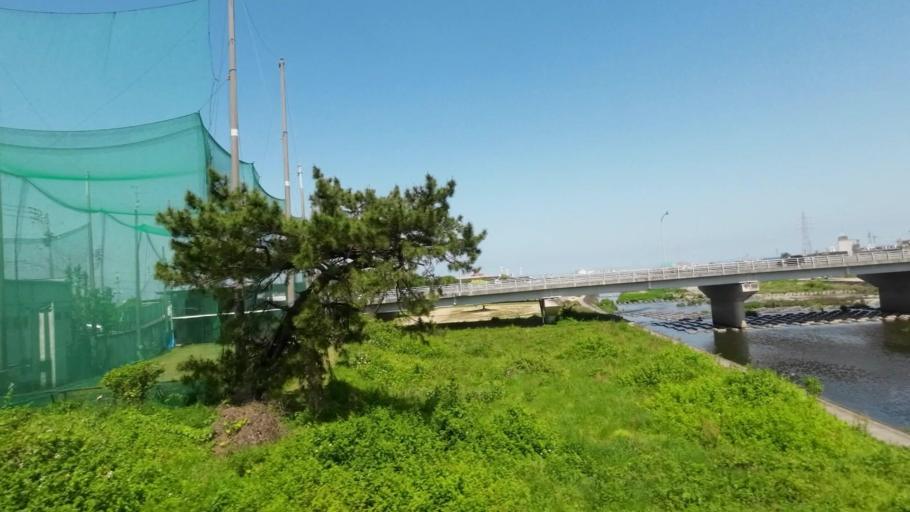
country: JP
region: Ehime
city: Niihama
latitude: 33.9545
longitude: 133.3020
